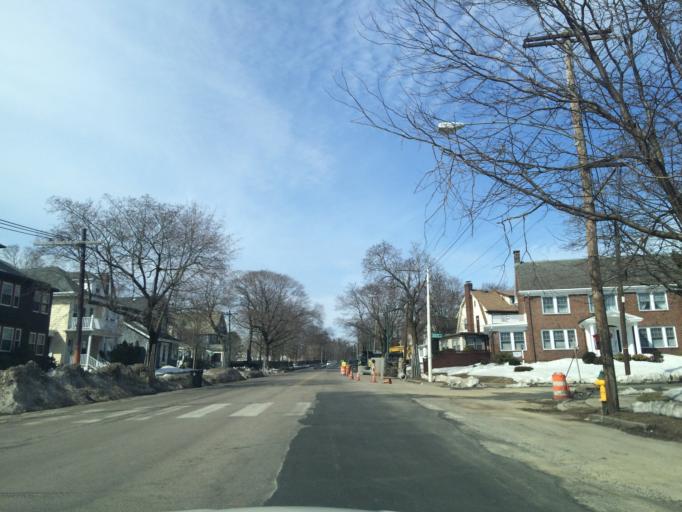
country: US
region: Massachusetts
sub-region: Middlesex County
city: Watertown
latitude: 42.3770
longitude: -71.1646
